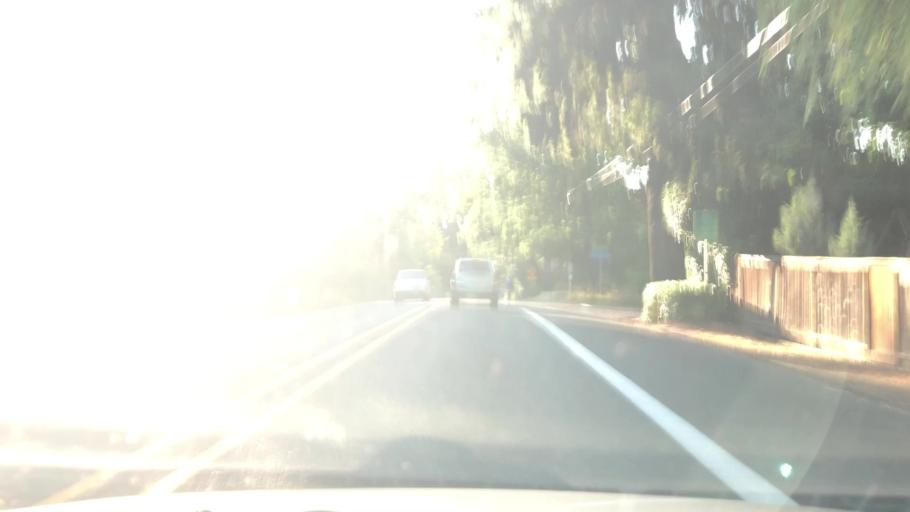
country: US
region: Oregon
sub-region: Clackamas County
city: Jennings Lodge
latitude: 45.3975
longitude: -122.6285
